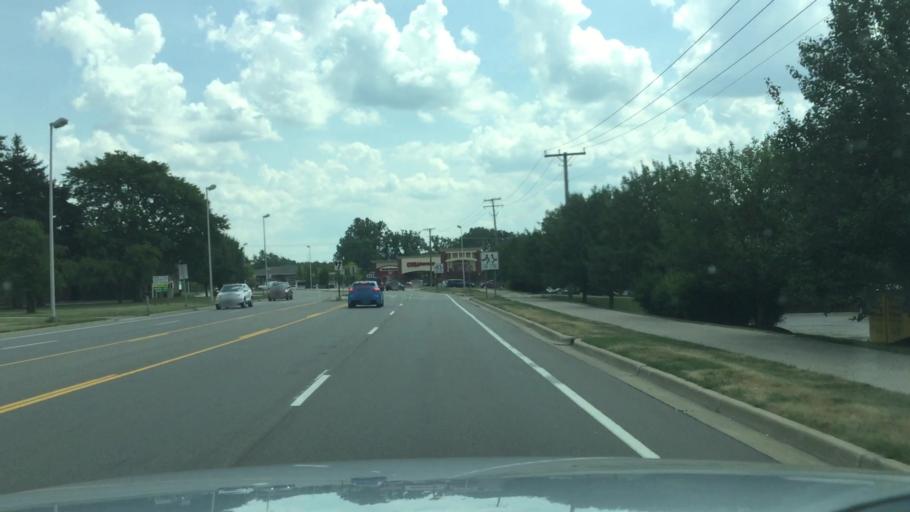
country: US
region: Michigan
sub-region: Washtenaw County
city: Ypsilanti
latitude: 42.2115
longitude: -83.6194
